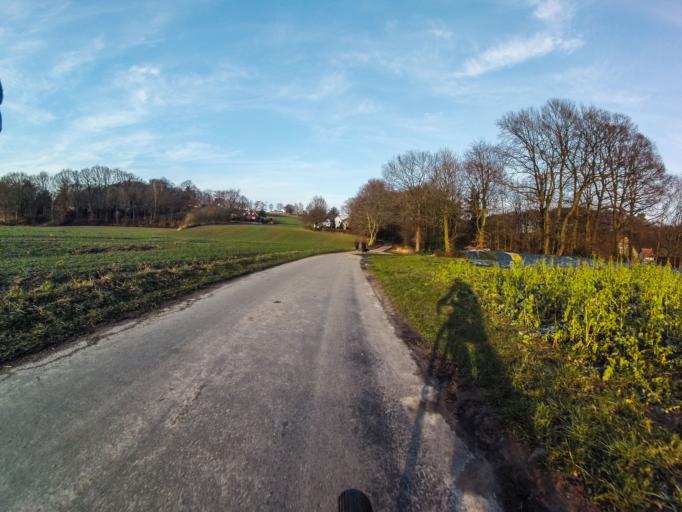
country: DE
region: North Rhine-Westphalia
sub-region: Regierungsbezirk Munster
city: Mettingen
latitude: 52.2719
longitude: 7.7943
